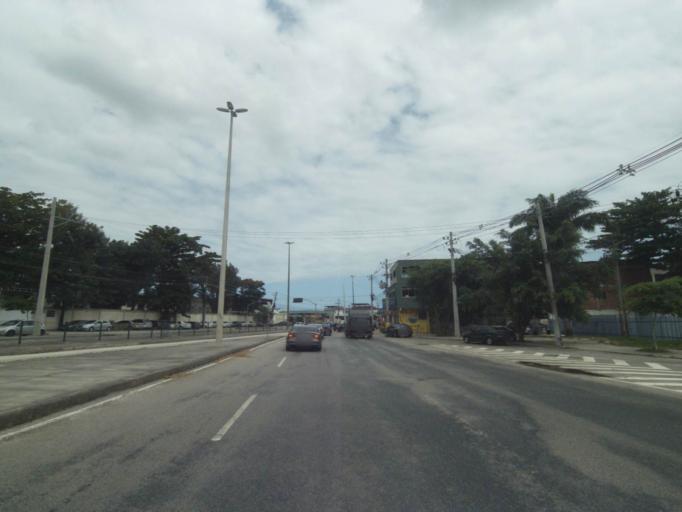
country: BR
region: Rio de Janeiro
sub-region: Sao Joao De Meriti
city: Sao Joao de Meriti
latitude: -22.9455
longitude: -43.3722
